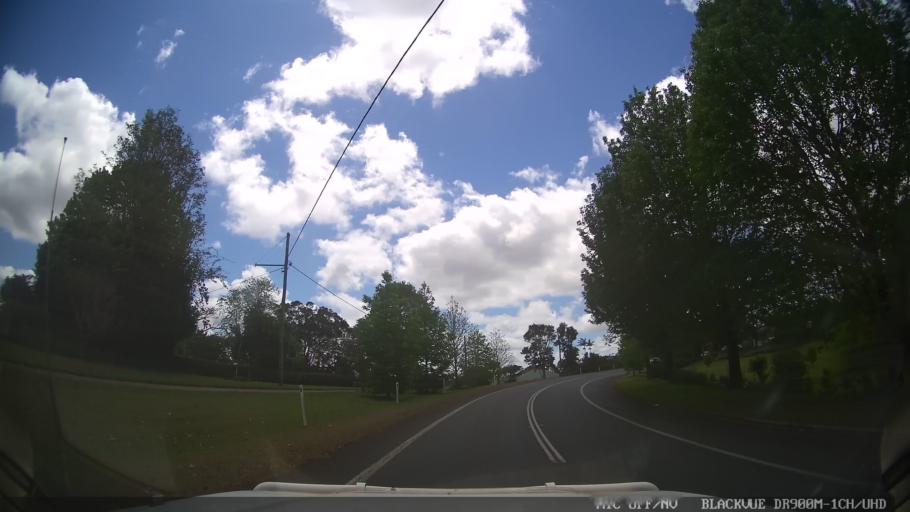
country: AU
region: Queensland
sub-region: Sunshine Coast
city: Nambour
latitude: -26.6643
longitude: 152.8798
